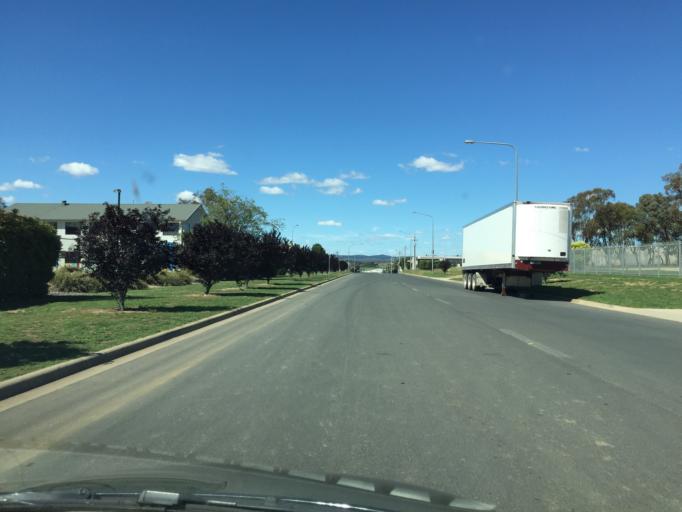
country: AU
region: Australian Capital Territory
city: Macarthur
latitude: -35.3947
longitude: 149.1617
